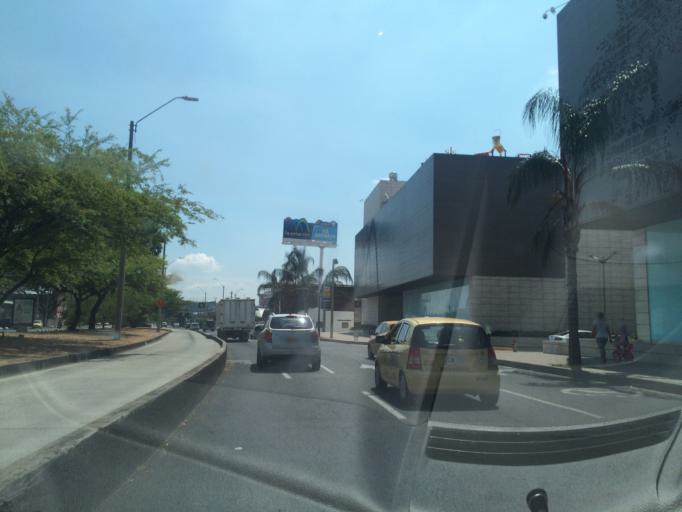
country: CO
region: Valle del Cauca
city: Cali
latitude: 3.4651
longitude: -76.5142
